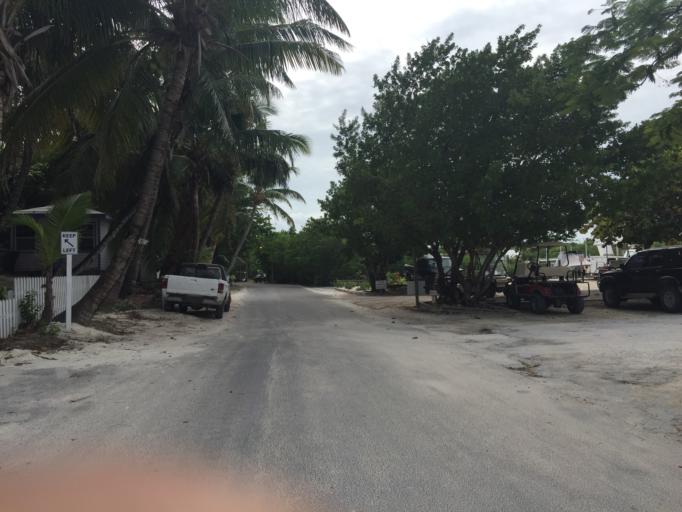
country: BS
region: Central Abaco
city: Marsh Harbour
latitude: 26.5359
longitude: -76.9582
